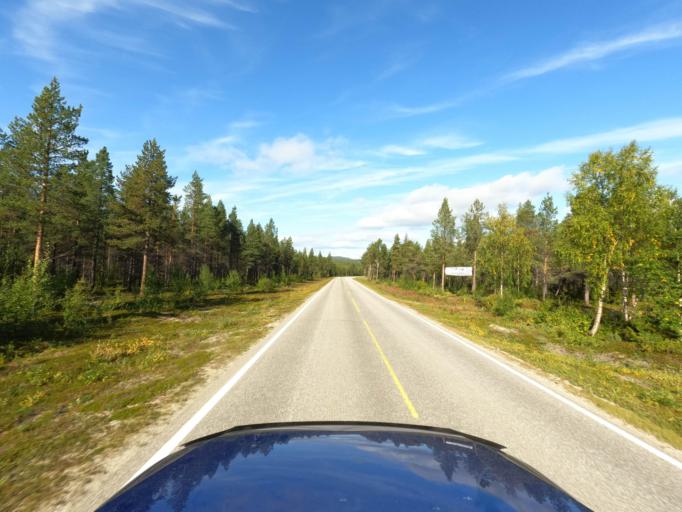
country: NO
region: Finnmark Fylke
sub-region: Porsanger
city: Lakselv
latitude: 69.8157
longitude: 25.1584
